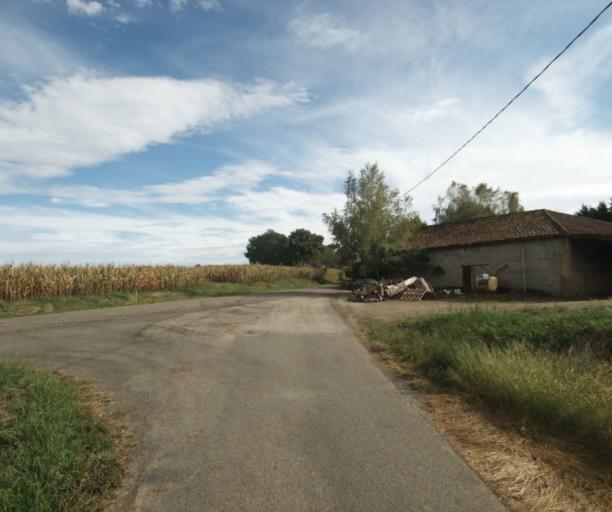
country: FR
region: Midi-Pyrenees
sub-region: Departement du Gers
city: Le Houga
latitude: 43.8762
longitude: -0.1689
